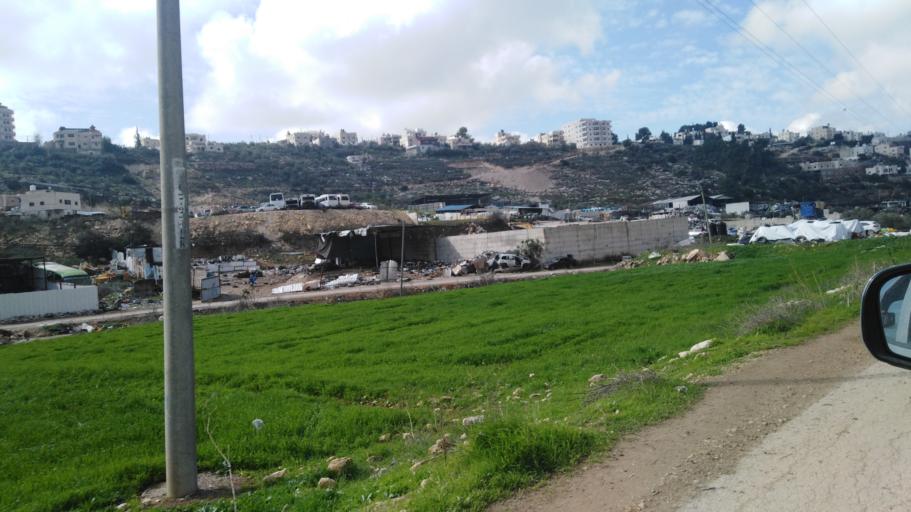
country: PS
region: West Bank
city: Idhna
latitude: 31.5563
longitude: 34.9888
